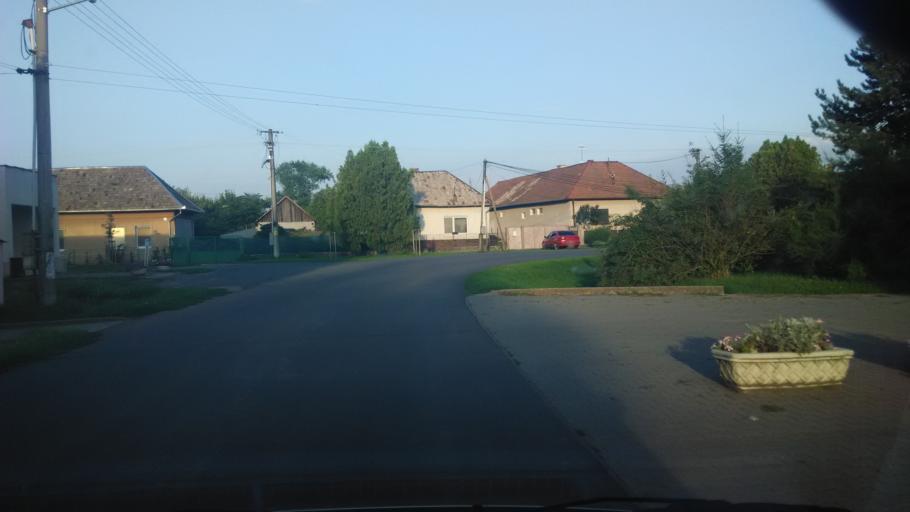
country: SK
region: Nitriansky
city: Sahy
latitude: 48.0197
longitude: 18.8072
